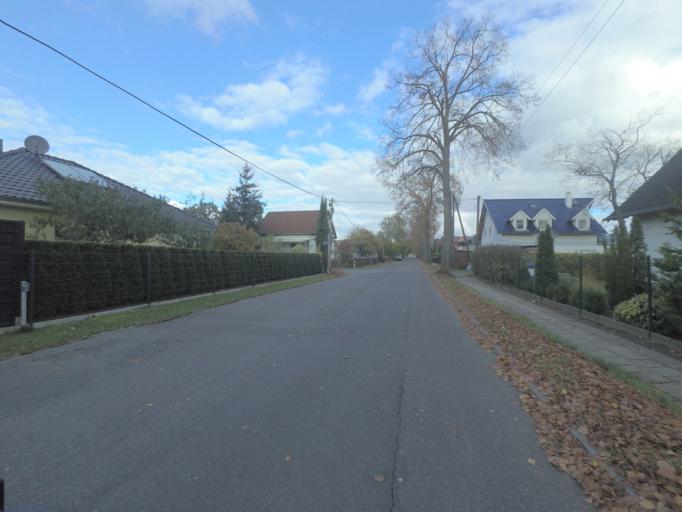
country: DE
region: Brandenburg
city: Ludwigsfelde
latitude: 52.2977
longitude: 13.2604
